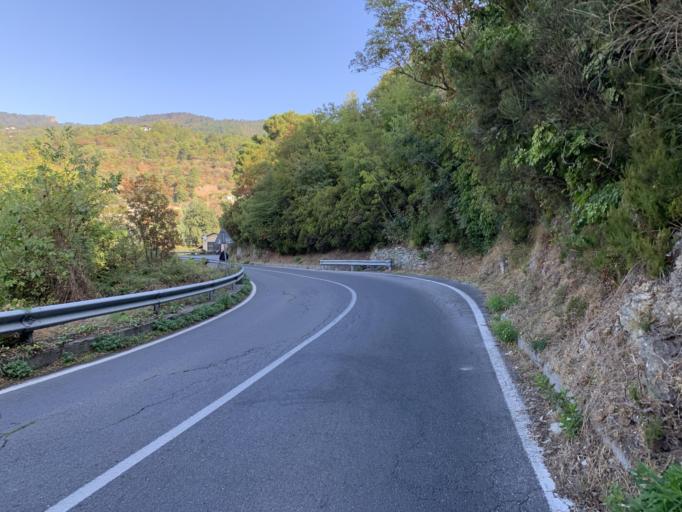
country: IT
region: Liguria
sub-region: Provincia di Savona
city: Magliolo
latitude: 44.1907
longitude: 8.2574
